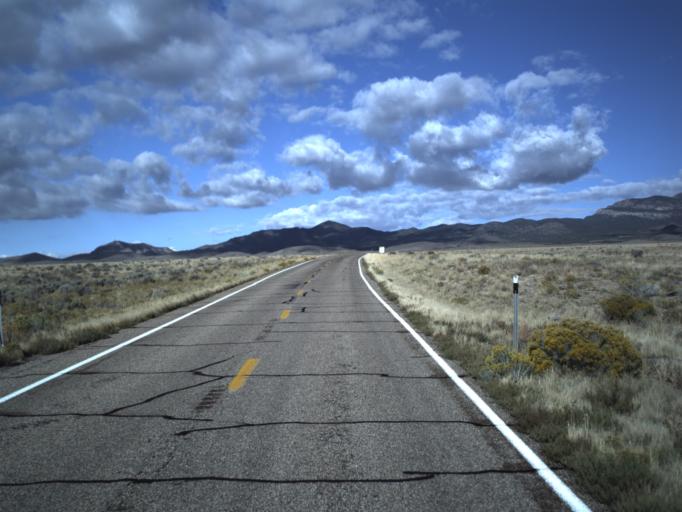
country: US
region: Utah
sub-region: Beaver County
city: Milford
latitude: 38.4422
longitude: -113.1701
